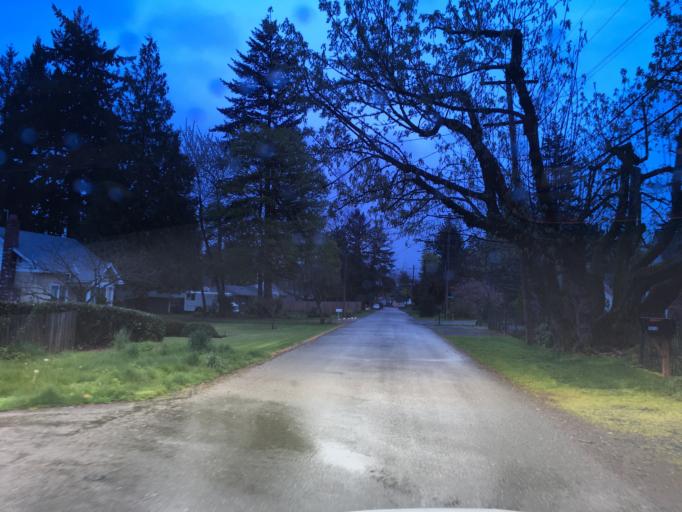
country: US
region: Oregon
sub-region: Multnomah County
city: Lents
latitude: 45.5582
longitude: -122.5921
